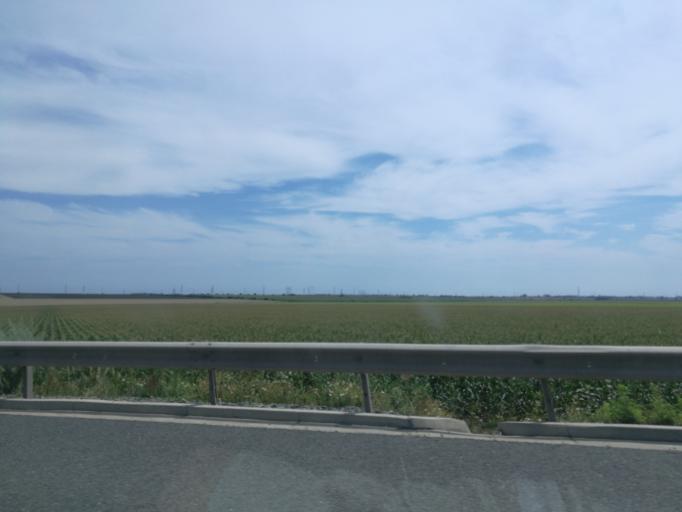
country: RO
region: Constanta
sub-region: Municipiul Constanta
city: Palazu Mare
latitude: 44.1971
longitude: 28.5520
